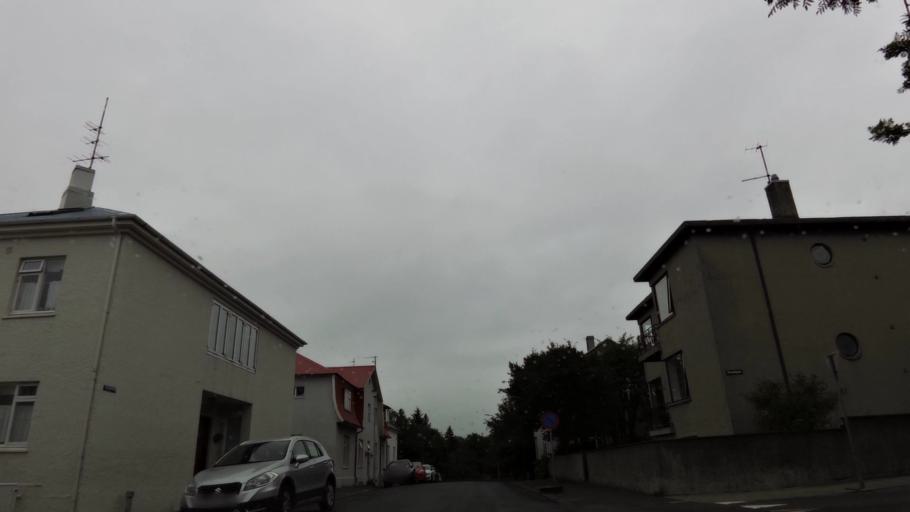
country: IS
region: Capital Region
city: Kopavogur
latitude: 64.1463
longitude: -21.9462
